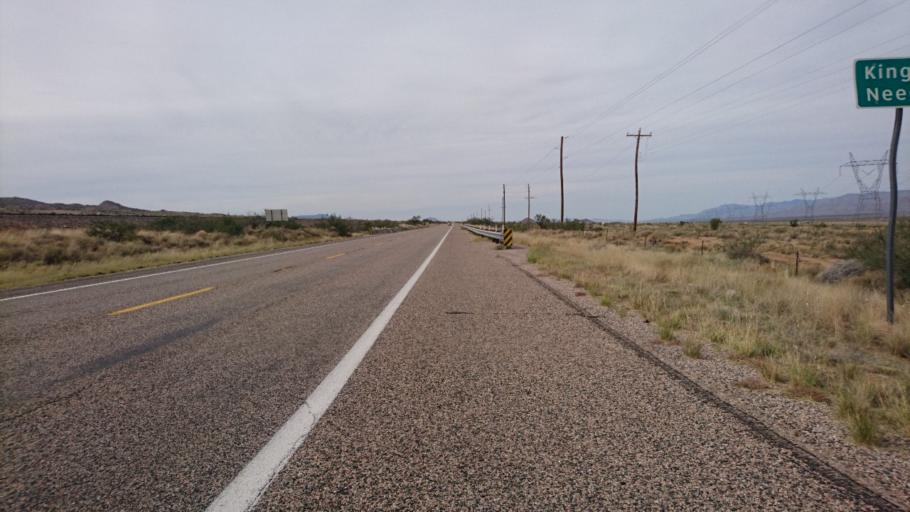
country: US
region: Arizona
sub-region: Mohave County
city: New Kingman-Butler
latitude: 35.3981
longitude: -113.7553
